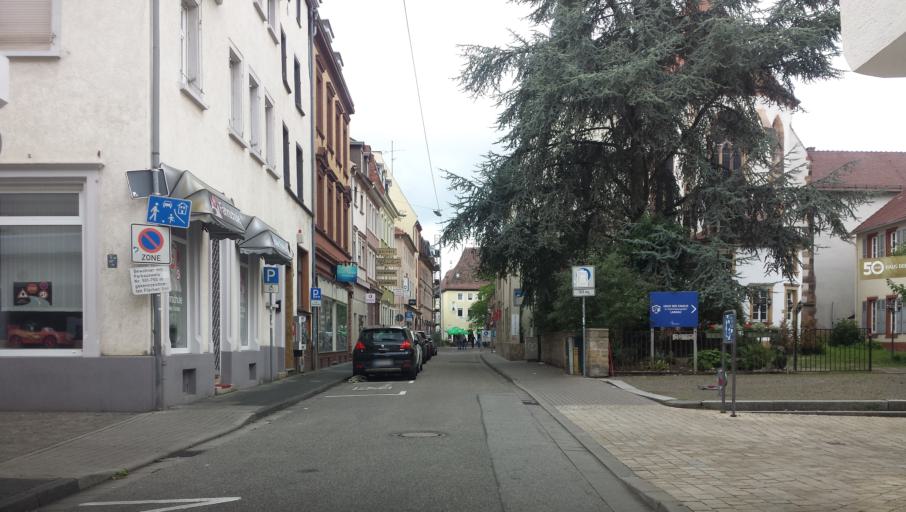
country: DE
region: Rheinland-Pfalz
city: Landau in der Pfalz
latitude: 49.1961
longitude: 8.1139
